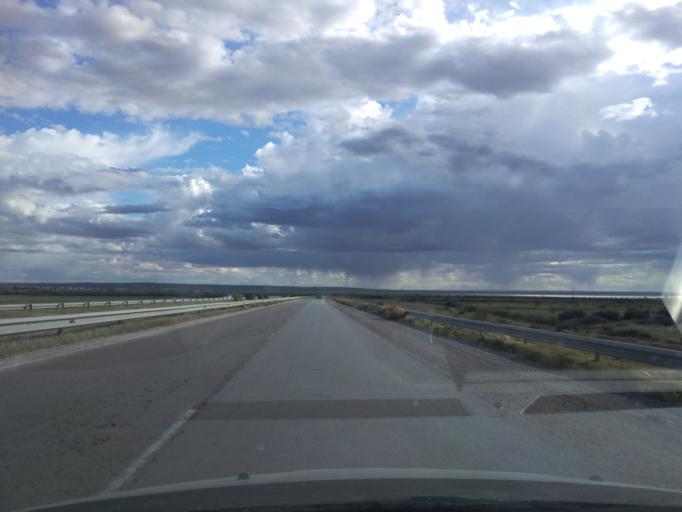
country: TN
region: Al Munastir
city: Manzil Kamil
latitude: 35.5145
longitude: 10.6265
